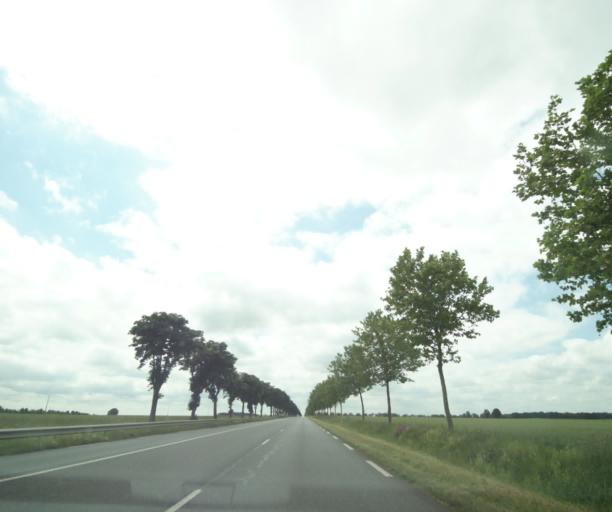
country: FR
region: Poitou-Charentes
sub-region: Departement des Deux-Sevres
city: Saint-Jean-de-Thouars
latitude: 46.9520
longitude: -0.2064
